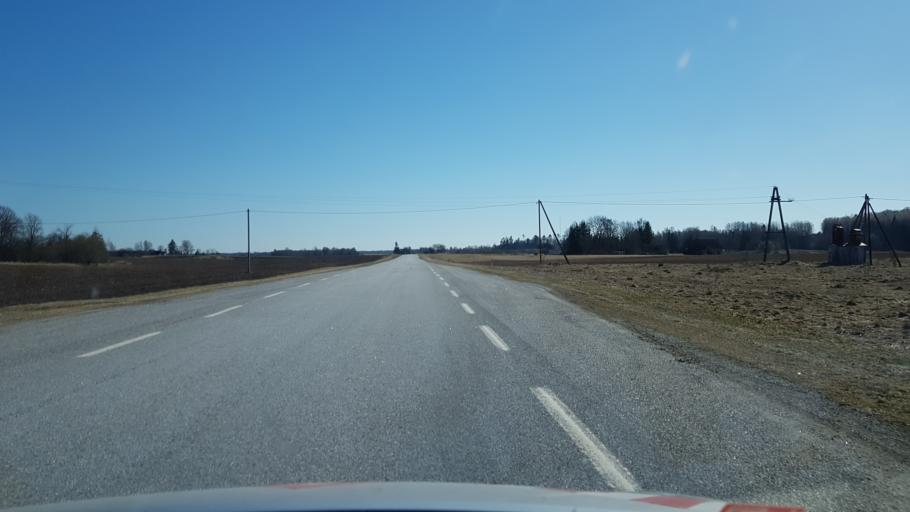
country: EE
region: Jaervamaa
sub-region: Koeru vald
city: Koeru
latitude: 59.0380
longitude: 26.0916
